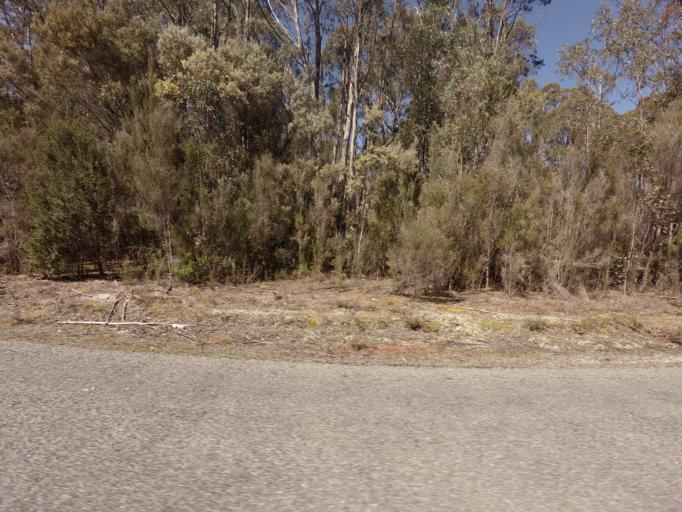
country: AU
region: Tasmania
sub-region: Huon Valley
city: Geeveston
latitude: -42.7656
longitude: 146.3972
